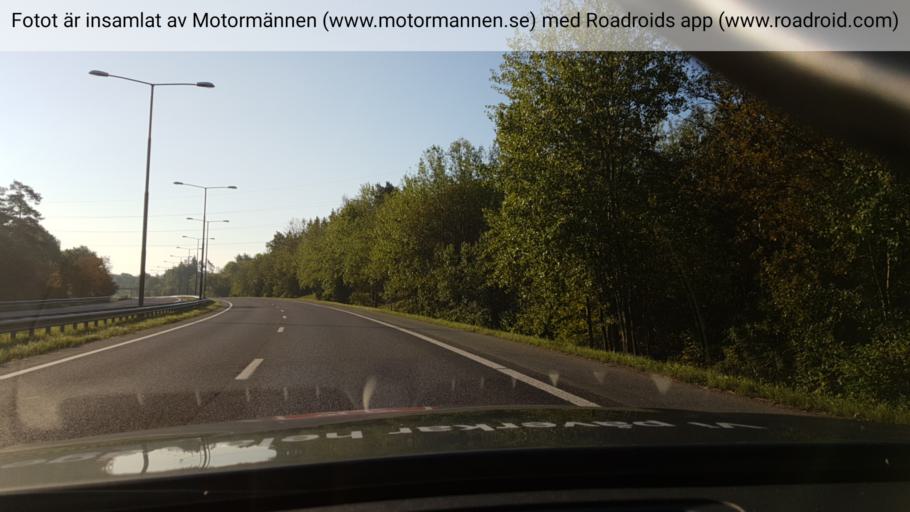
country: SE
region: Stockholm
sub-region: Stockholms Kommun
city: Arsta
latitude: 59.2618
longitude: 18.0656
